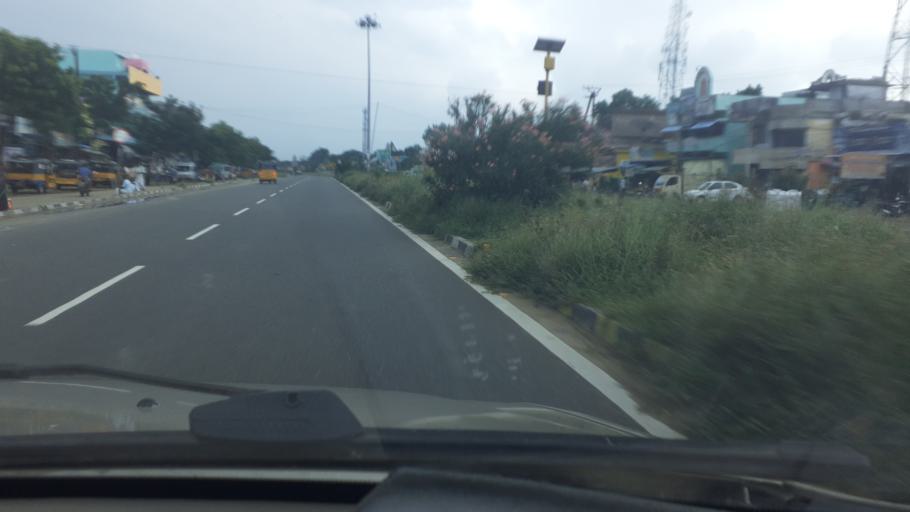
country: IN
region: Tamil Nadu
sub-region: Madurai
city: Kallupatti
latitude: 9.6983
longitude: 77.9721
